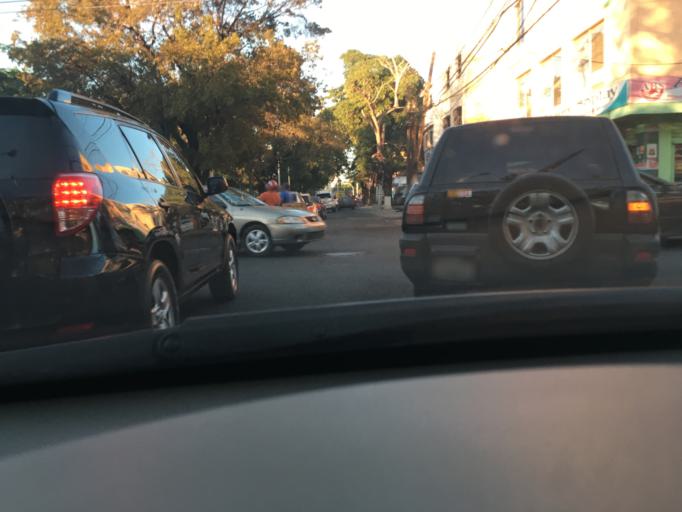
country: DO
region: Nacional
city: San Carlos
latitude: 18.4791
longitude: -69.9056
